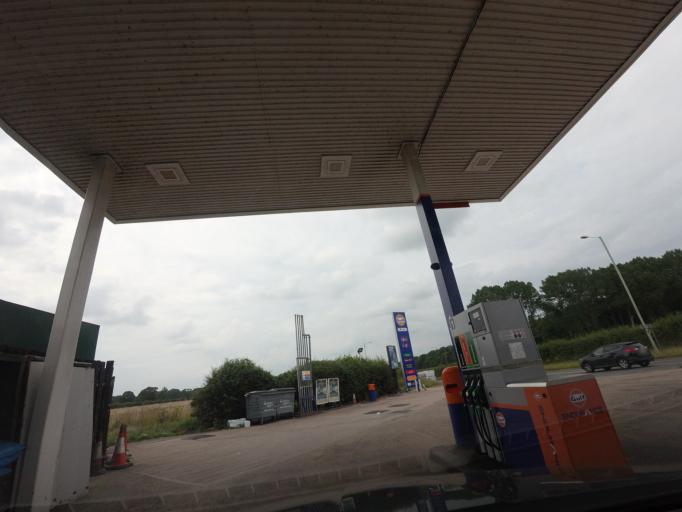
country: GB
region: England
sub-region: Shropshire
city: Tong
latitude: 52.6706
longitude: -2.3095
